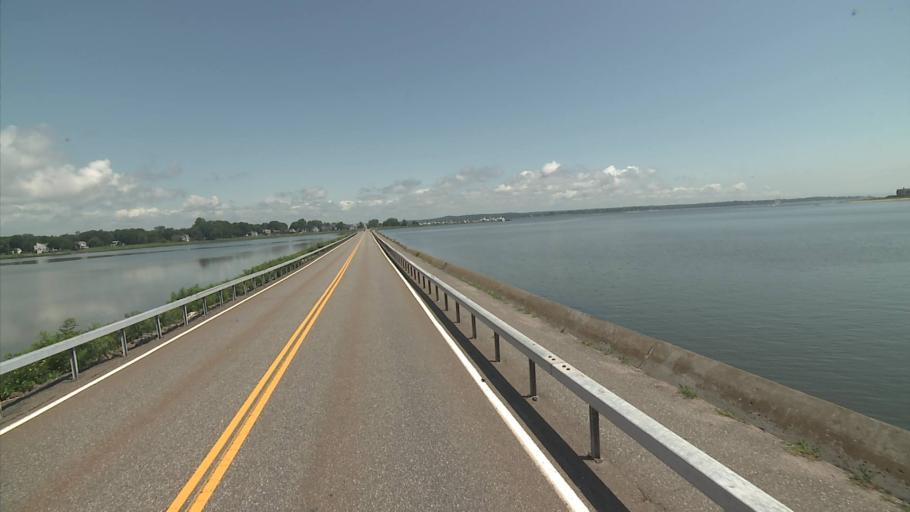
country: US
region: Connecticut
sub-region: Middlesex County
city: Old Saybrook Center
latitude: 41.2753
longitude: -72.3565
